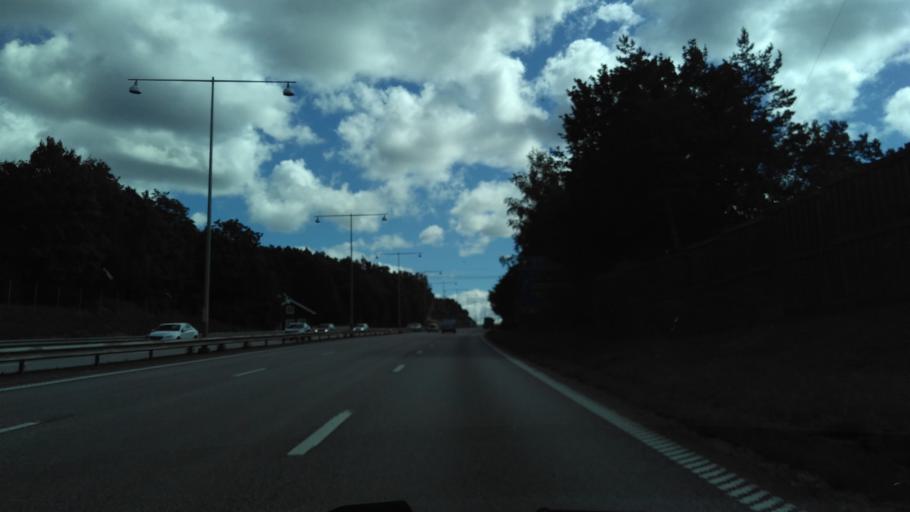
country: SE
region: Vaestra Goetaland
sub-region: Molndal
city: Moelndal
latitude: 57.6834
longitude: 12.0154
